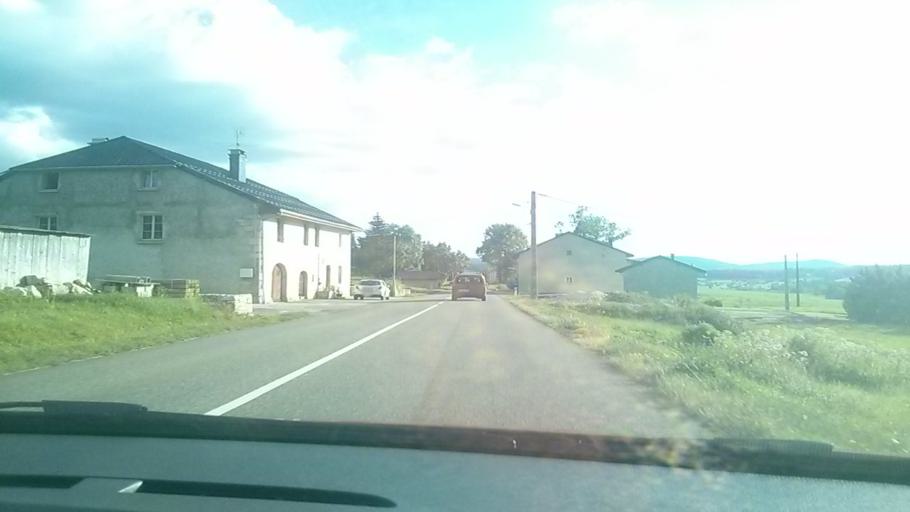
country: FR
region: Franche-Comte
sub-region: Departement du Jura
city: Les Rousses
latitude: 46.5031
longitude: 6.1027
